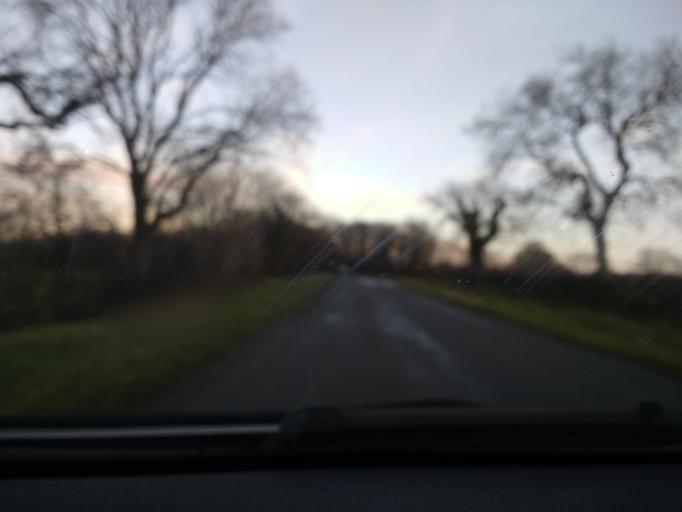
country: GB
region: England
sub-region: Cumbria
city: Carlisle
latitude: 54.7326
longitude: -2.9368
